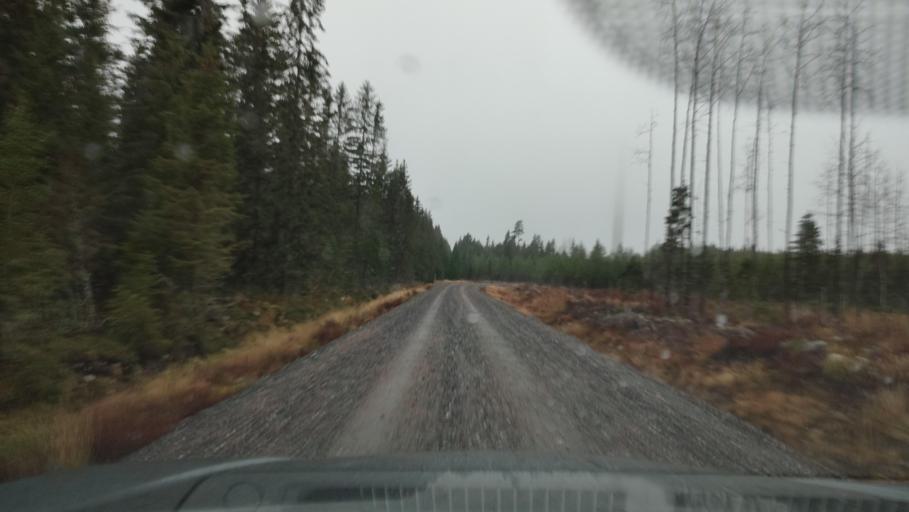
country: FI
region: Southern Ostrobothnia
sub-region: Suupohja
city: Karijoki
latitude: 62.1782
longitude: 21.7211
